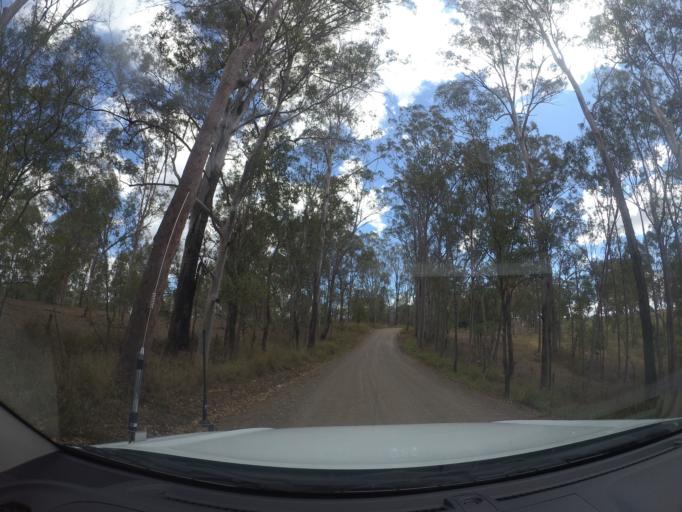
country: AU
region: Queensland
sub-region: Logan
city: Cedar Vale
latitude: -27.8956
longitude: 152.9925
